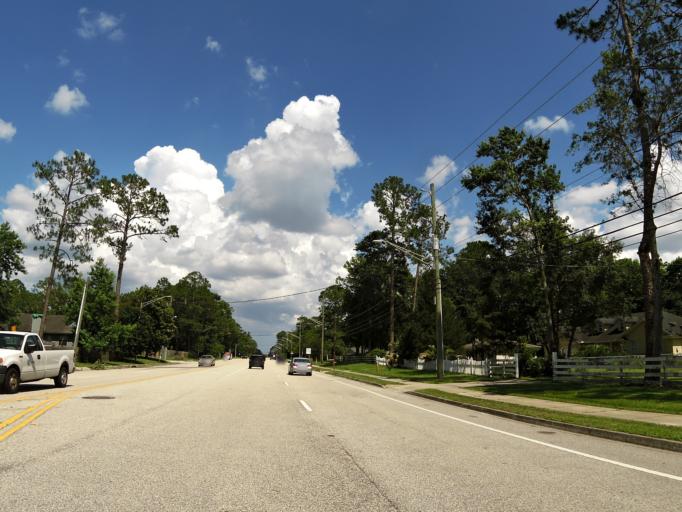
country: US
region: Florida
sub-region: Saint Johns County
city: Fruit Cove
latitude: 30.1477
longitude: -81.5718
